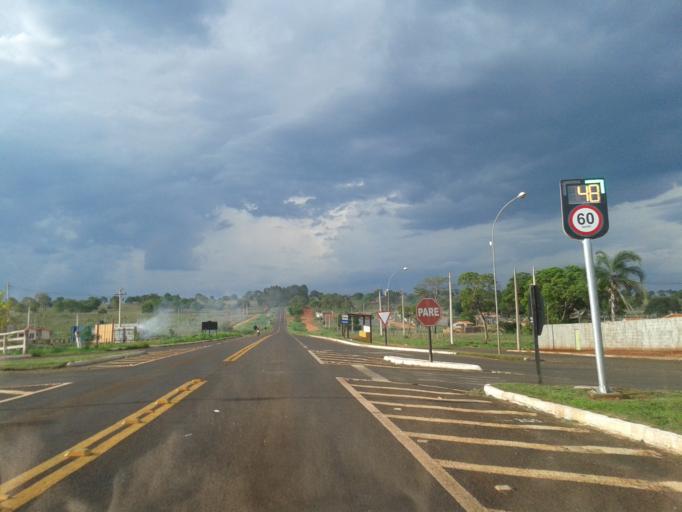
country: BR
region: Goias
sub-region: Quirinopolis
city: Quirinopolis
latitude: -18.9050
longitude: -50.6613
